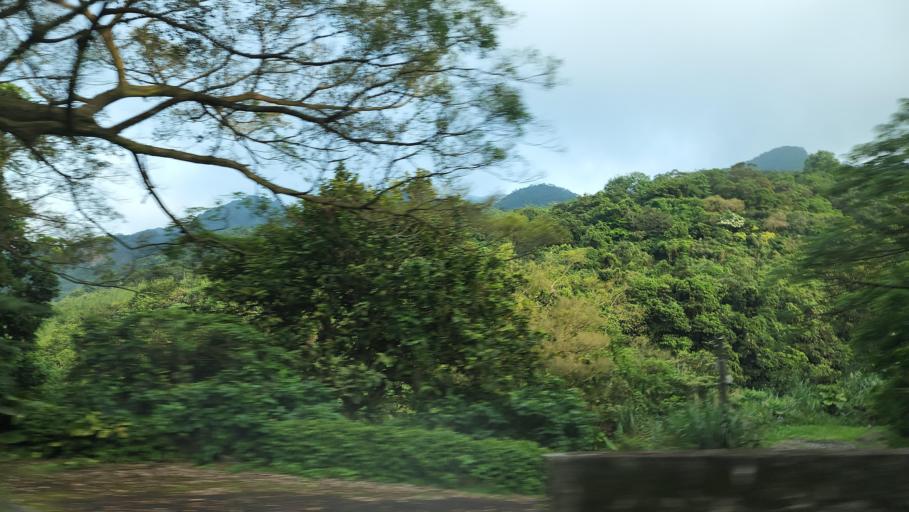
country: TW
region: Taiwan
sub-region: Keelung
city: Keelung
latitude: 25.1594
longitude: 121.6479
